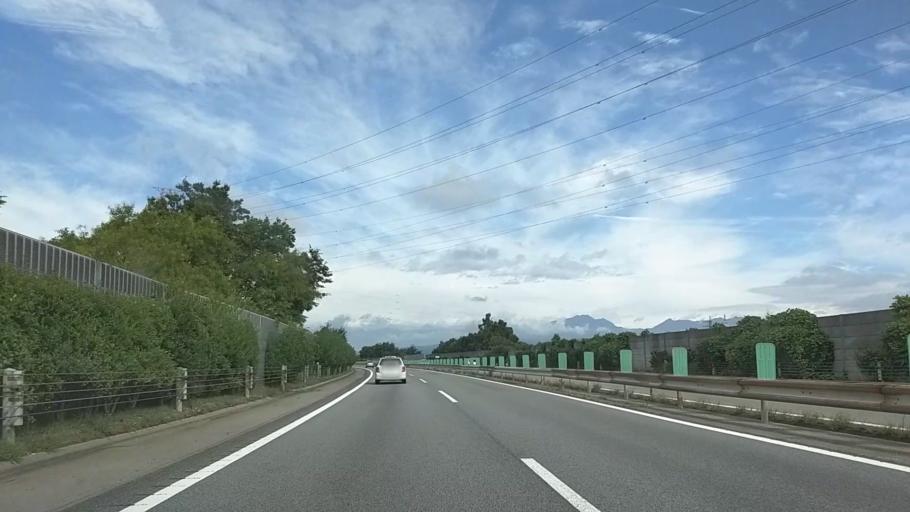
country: JP
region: Yamanashi
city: Kofu-shi
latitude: 35.6256
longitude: 138.5464
